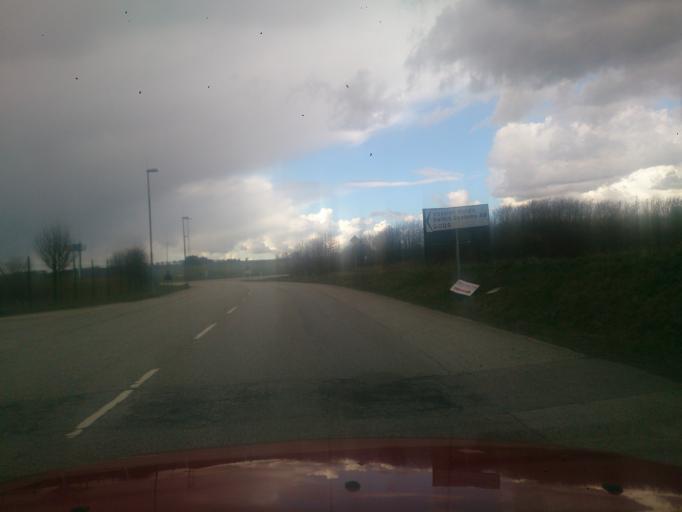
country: SE
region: Skane
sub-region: Ystads Kommun
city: Ystad
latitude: 55.4308
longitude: 13.7767
